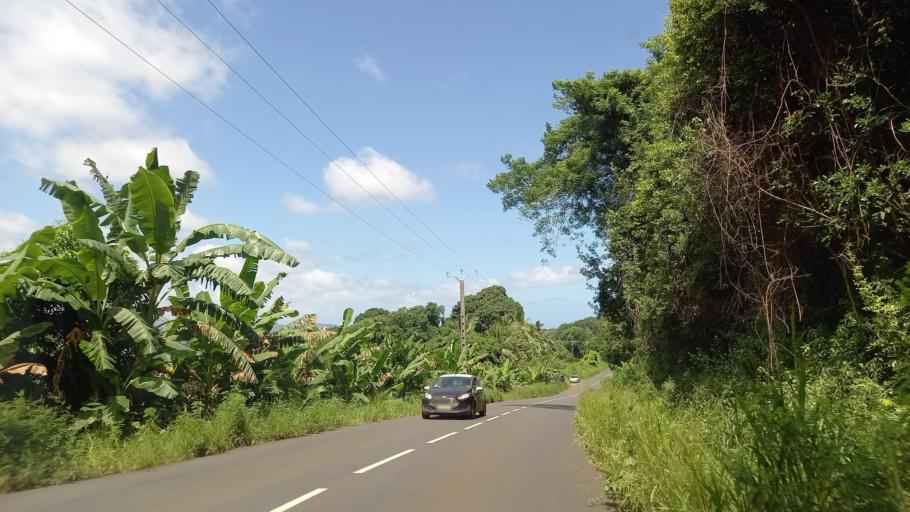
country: YT
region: Acoua
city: Acoua
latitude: -12.7410
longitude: 45.0544
